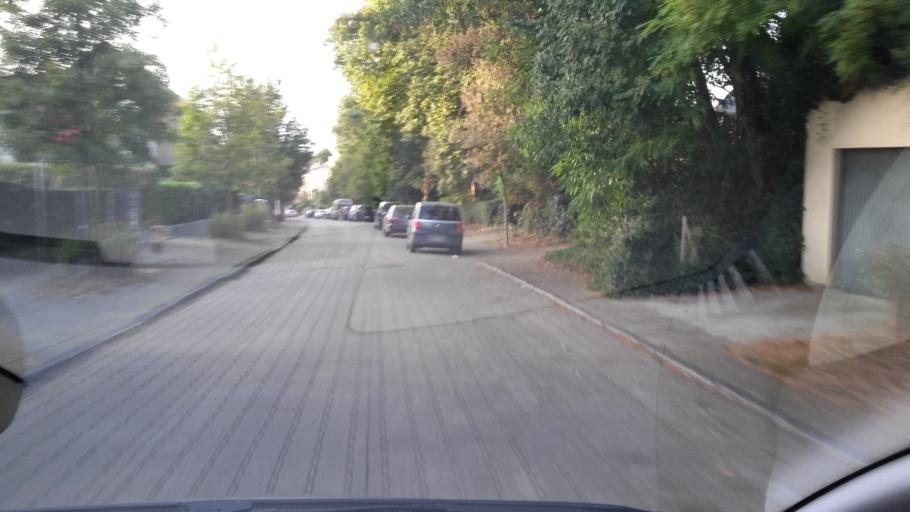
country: BE
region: Flanders
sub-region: Provincie Vlaams-Brabant
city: Hoeilaart
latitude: 50.8017
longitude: 4.4066
